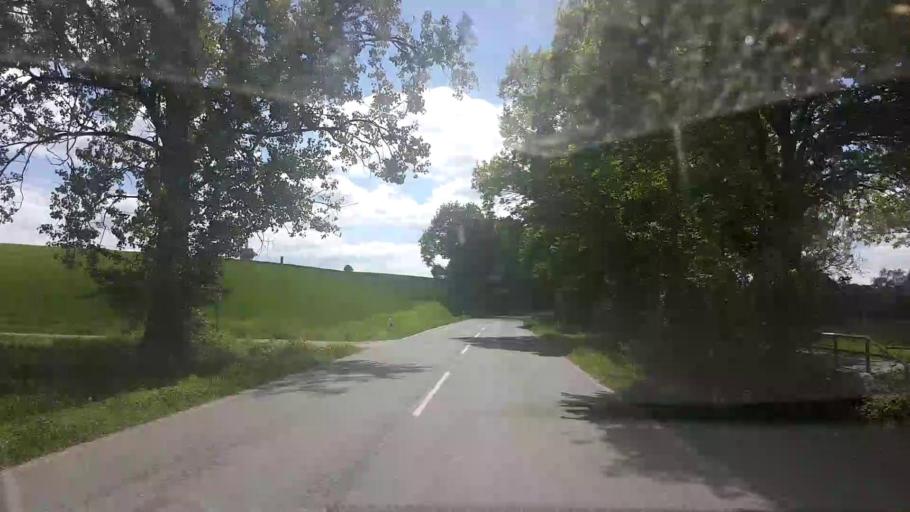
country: DE
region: Bavaria
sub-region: Upper Franconia
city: Grossheirath
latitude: 50.1718
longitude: 10.9433
